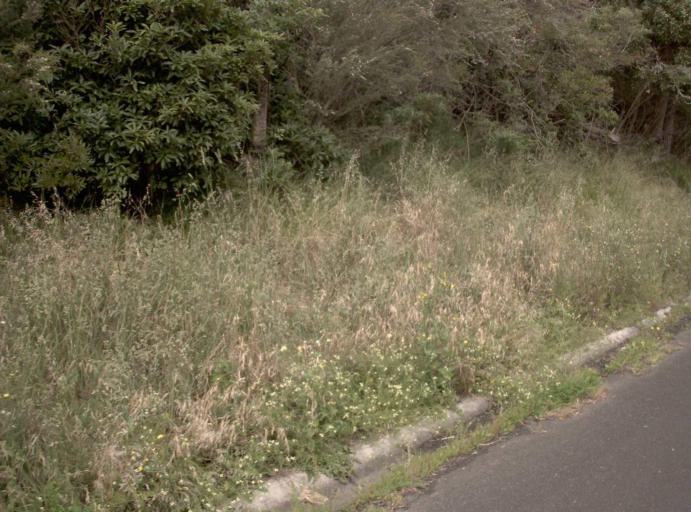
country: AU
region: Victoria
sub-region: Cardinia
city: Bunyip
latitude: -38.0915
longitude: 145.8323
